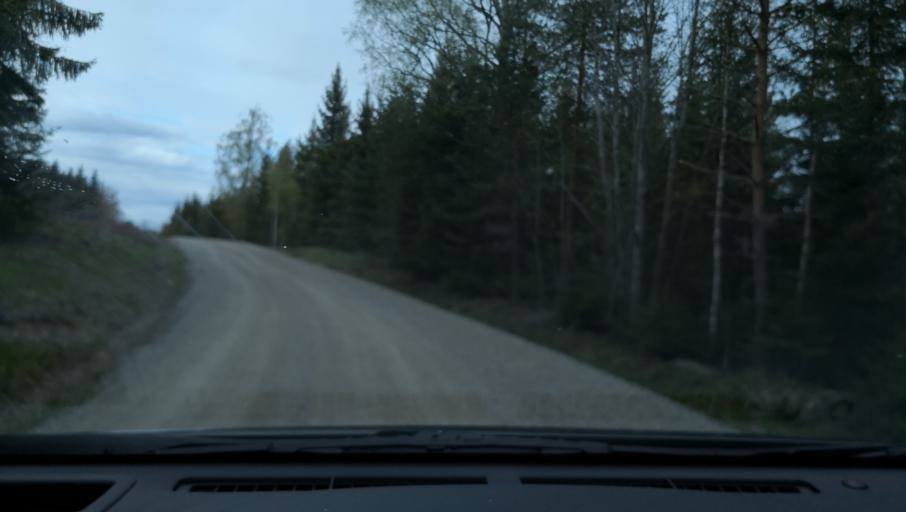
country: SE
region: Dalarna
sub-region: Saters Kommun
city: Saeter
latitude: 60.2054
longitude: 15.7449
